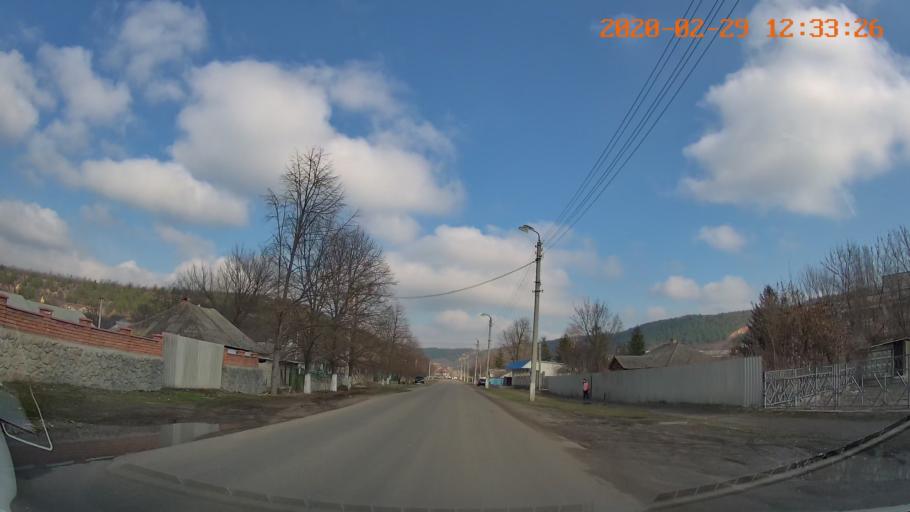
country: MD
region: Telenesti
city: Camenca
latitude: 48.0352
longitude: 28.7043
